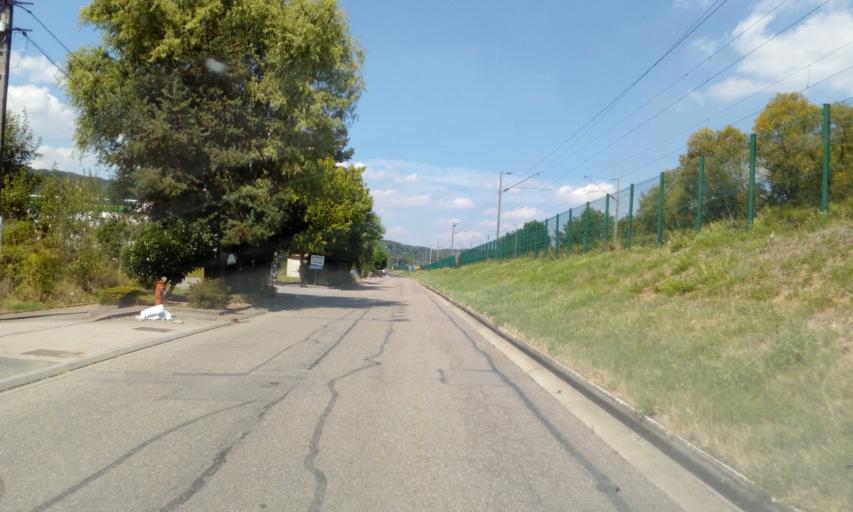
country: FR
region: Lorraine
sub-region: Departement de Meurthe-et-Moselle
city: Maidieres
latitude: 48.9090
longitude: 6.0449
